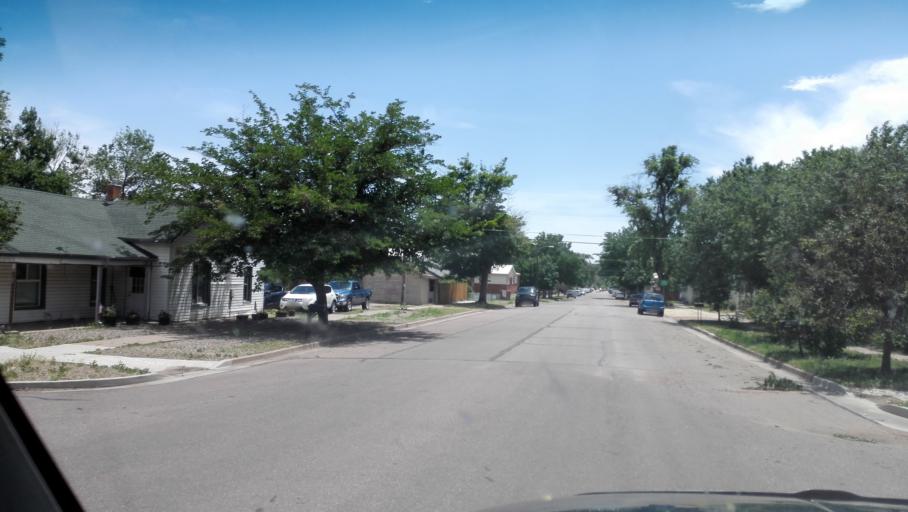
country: US
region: Colorado
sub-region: Fremont County
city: Canon City
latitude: 38.4438
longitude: -105.2433
